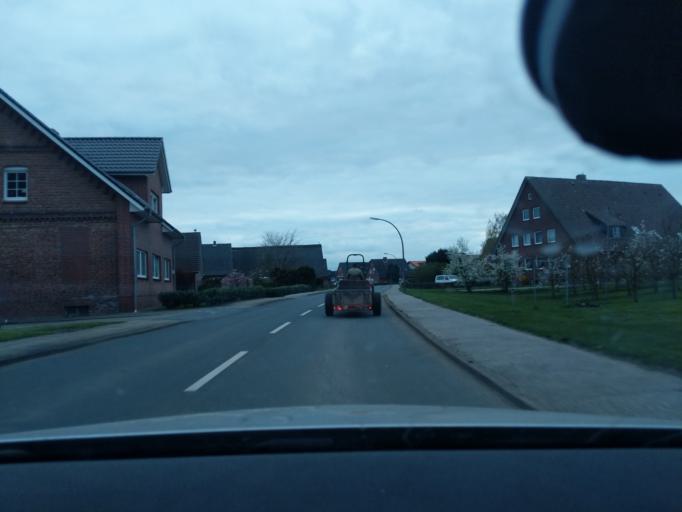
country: DE
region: Lower Saxony
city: Neu Wulmstorf
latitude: 53.5136
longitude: 9.8033
